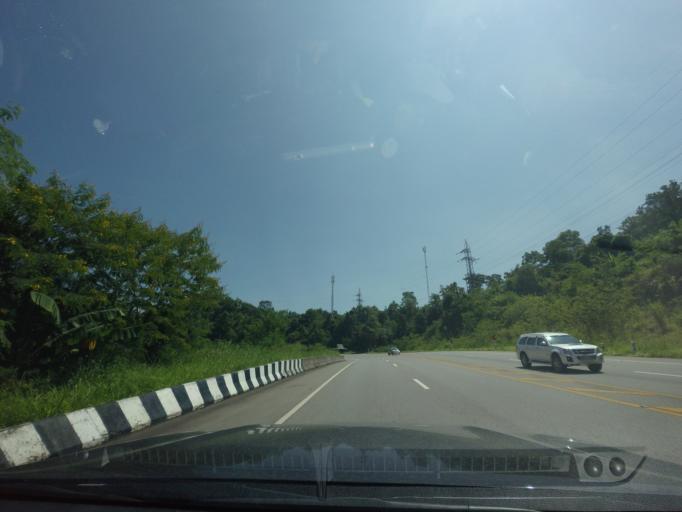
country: TH
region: Phetchabun
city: Lom Sak
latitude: 16.7777
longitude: 101.1113
